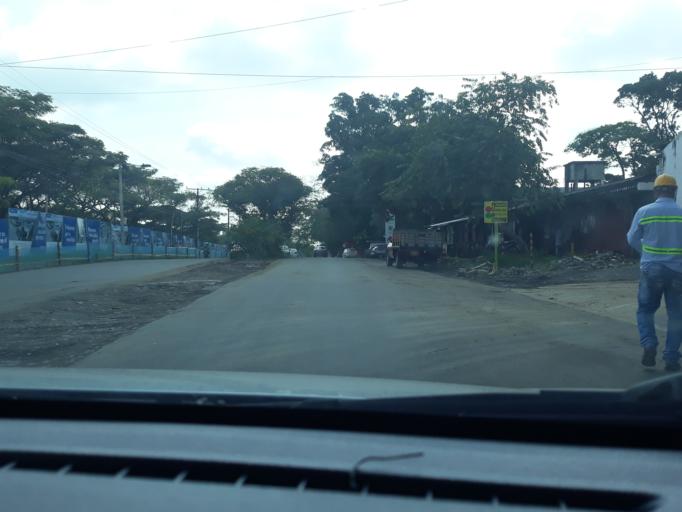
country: CO
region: Valle del Cauca
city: Cali
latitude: 3.3589
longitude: -76.5224
